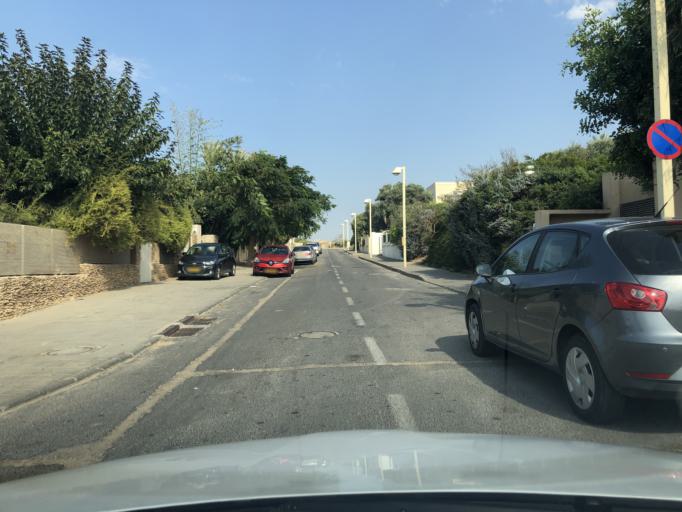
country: IL
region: Tel Aviv
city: Kefar Shemaryahu
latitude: 32.2127
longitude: 34.8153
